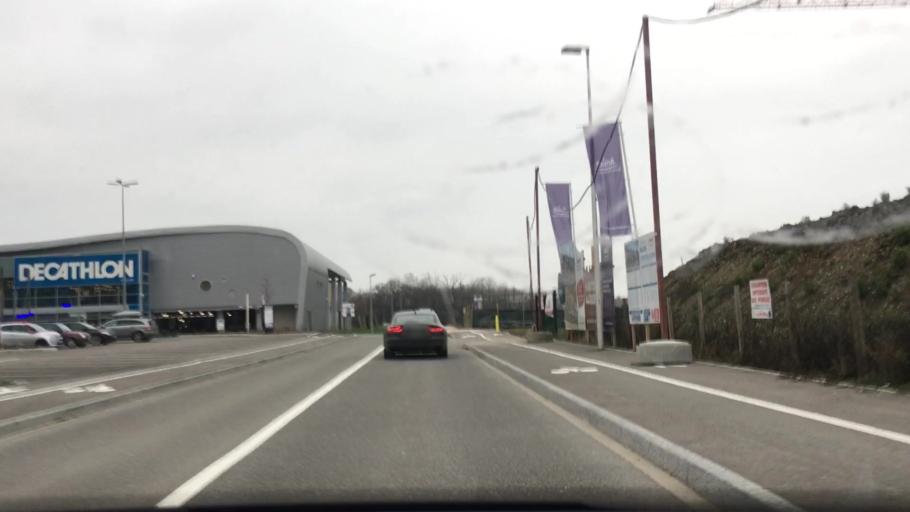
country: FR
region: Rhone-Alpes
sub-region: Departement de la Haute-Savoie
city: Marin
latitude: 46.3897
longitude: 6.5222
